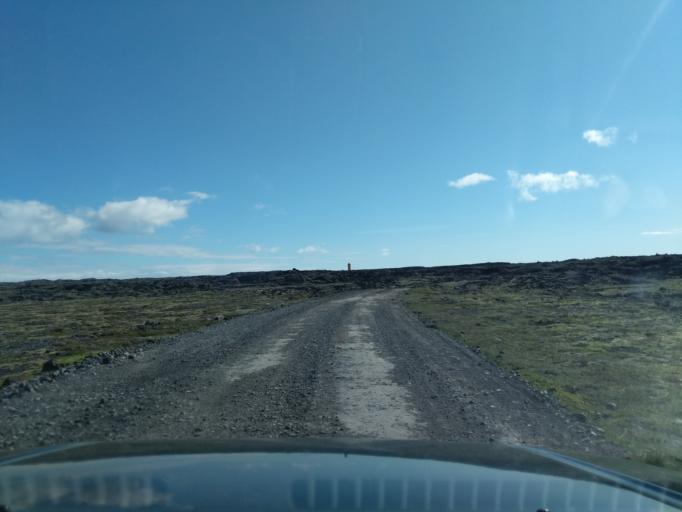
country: IS
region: West
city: Olafsvik
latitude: 64.8700
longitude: -24.0344
